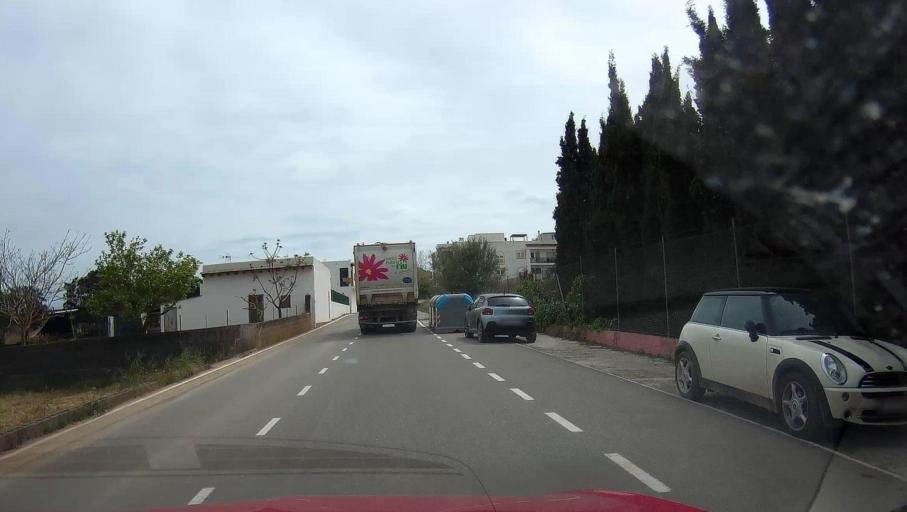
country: ES
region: Balearic Islands
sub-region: Illes Balears
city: Ibiza
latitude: 39.0012
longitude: 1.4292
